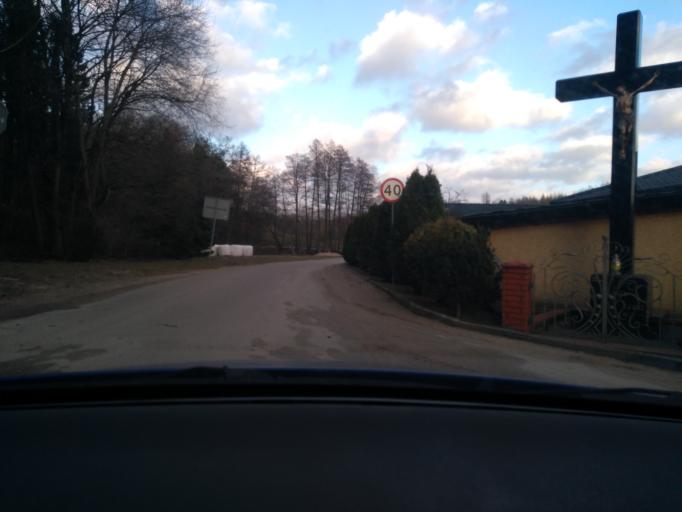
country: PL
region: Pomeranian Voivodeship
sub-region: Powiat kartuski
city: Przodkowo
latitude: 54.4150
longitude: 18.2466
